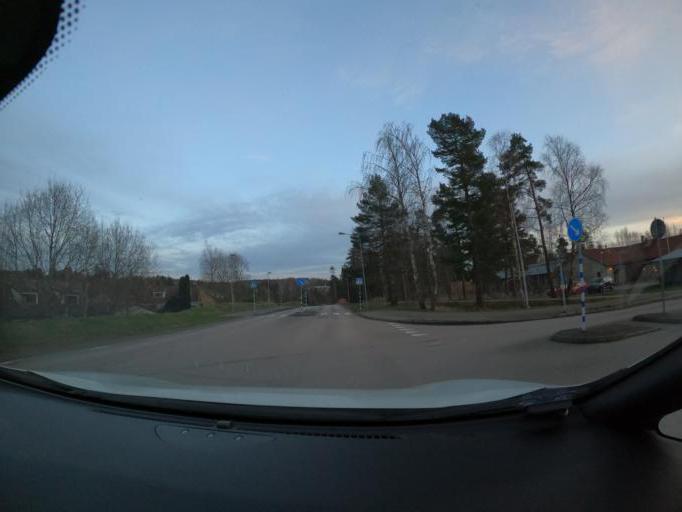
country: SE
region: Vaestra Goetaland
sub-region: Harryda Kommun
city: Molnlycke
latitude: 57.6521
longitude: 12.1388
